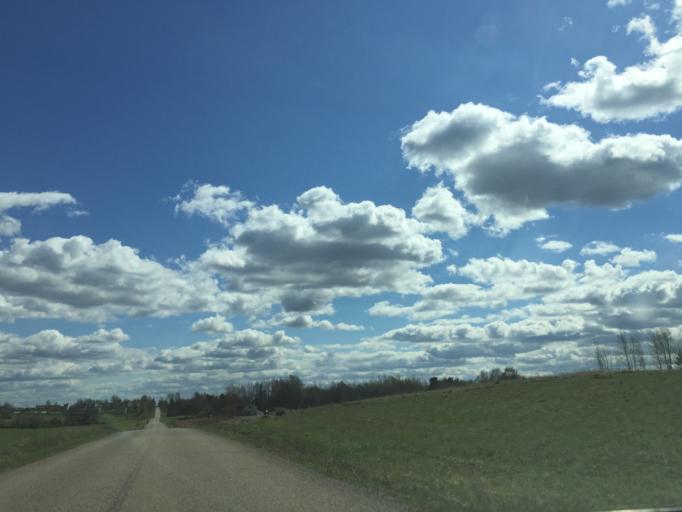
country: LV
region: Rezekne
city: Rezekne
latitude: 56.5733
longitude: 27.1348
